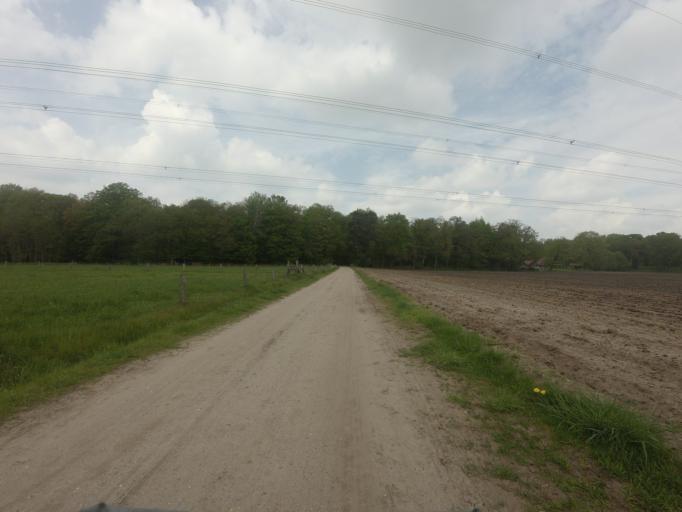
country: NL
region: Overijssel
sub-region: Gemeente Hof van Twente
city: Delden
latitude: 52.2477
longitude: 6.7202
